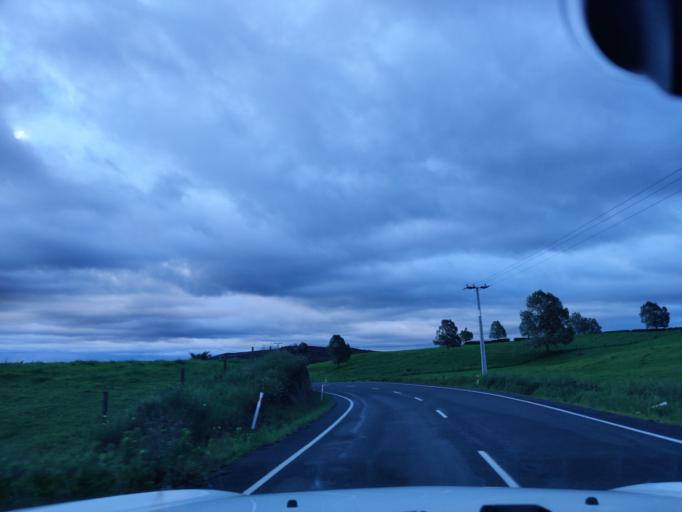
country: NZ
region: Waikato
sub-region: South Waikato District
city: Tokoroa
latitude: -38.1637
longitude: 175.7669
